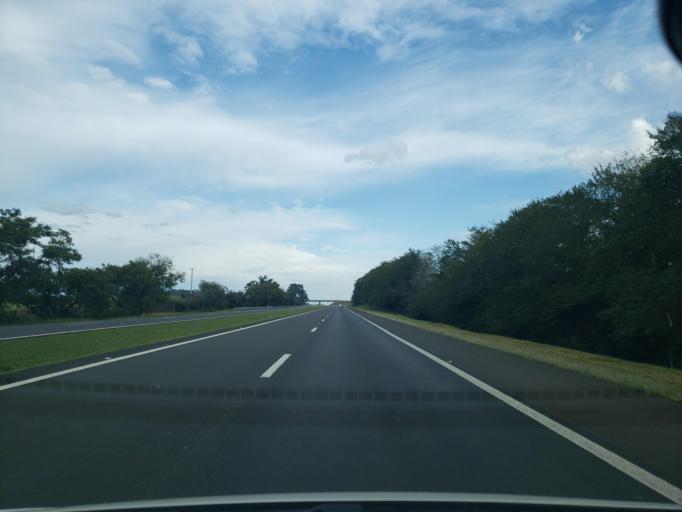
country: BR
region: Sao Paulo
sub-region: Itirapina
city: Itirapina
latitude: -22.2670
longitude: -47.9275
